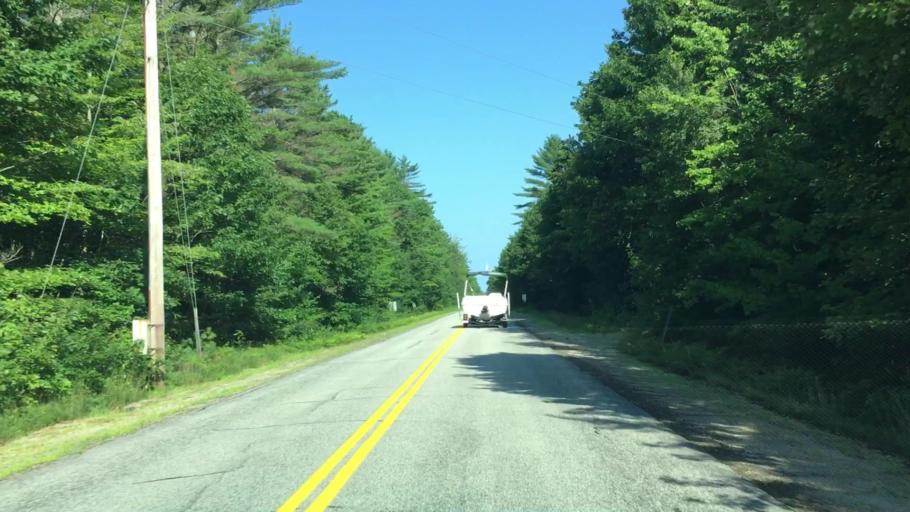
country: US
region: Maine
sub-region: Androscoggin County
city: Poland
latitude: 44.0442
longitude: -70.3568
